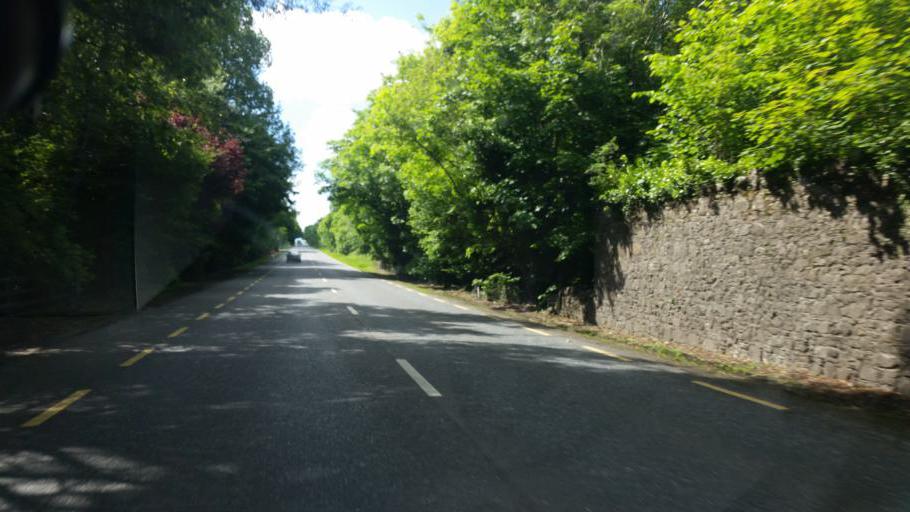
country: IE
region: Leinster
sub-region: Uibh Fhaili
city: Tullamore
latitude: 53.3091
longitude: -7.4984
